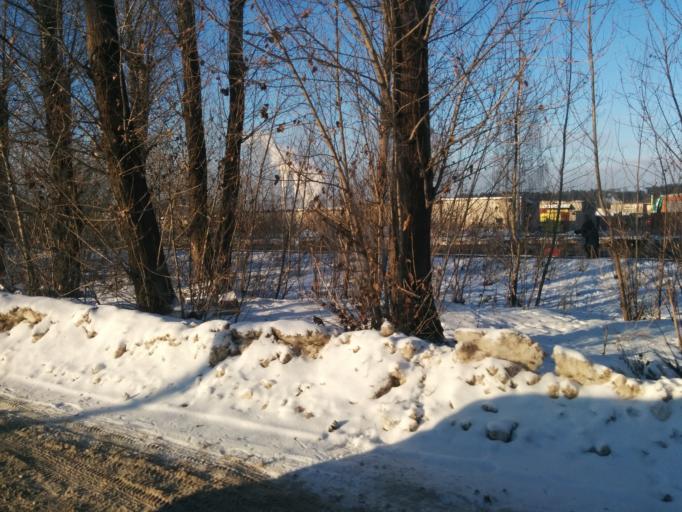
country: RU
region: Perm
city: Overyata
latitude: 58.0137
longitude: 55.9561
